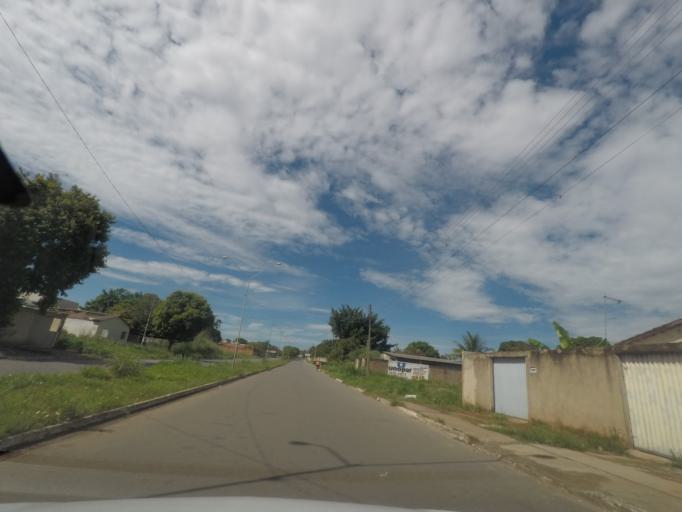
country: BR
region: Goias
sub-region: Aparecida De Goiania
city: Aparecida de Goiania
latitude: -16.8168
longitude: -49.2898
